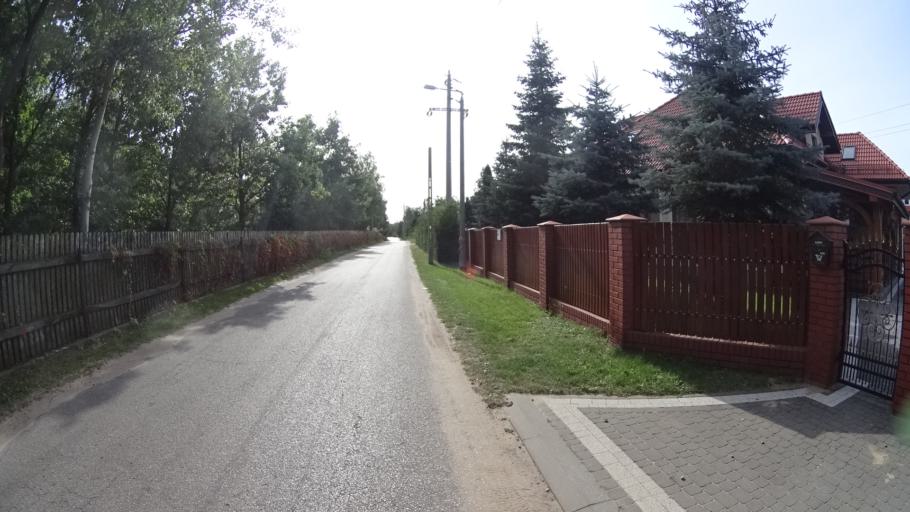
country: PL
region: Masovian Voivodeship
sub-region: Powiat legionowski
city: Serock
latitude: 52.4882
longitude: 21.0843
